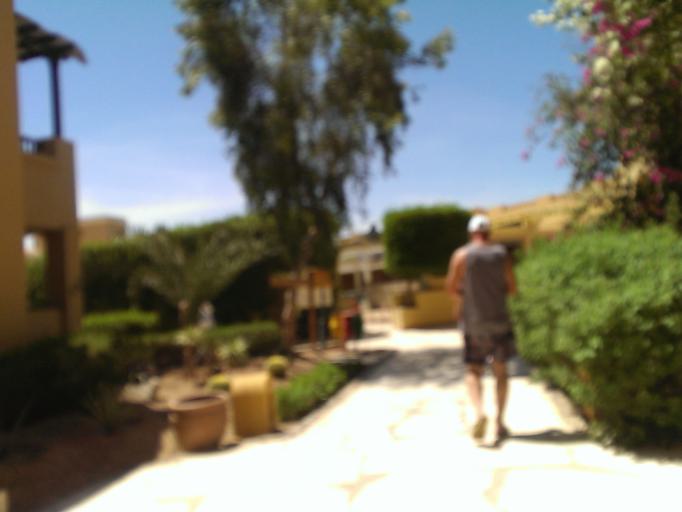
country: EG
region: Red Sea
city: El Gouna
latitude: 27.3996
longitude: 33.6728
